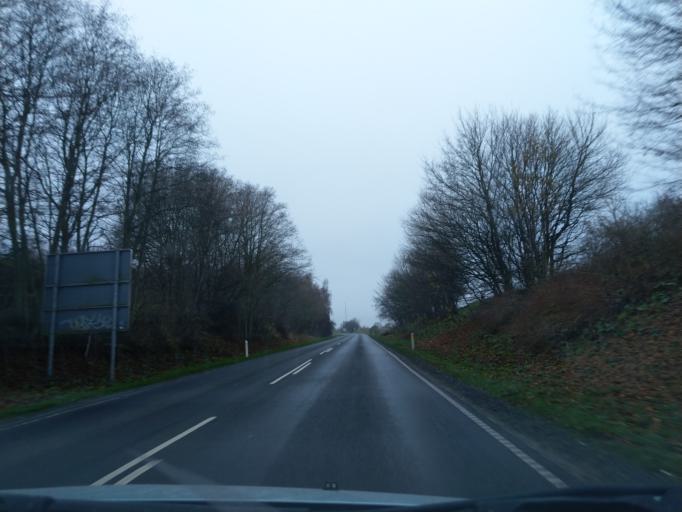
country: DK
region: Zealand
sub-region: Vordingborg Kommune
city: Praesto
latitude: 55.1158
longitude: 12.0295
